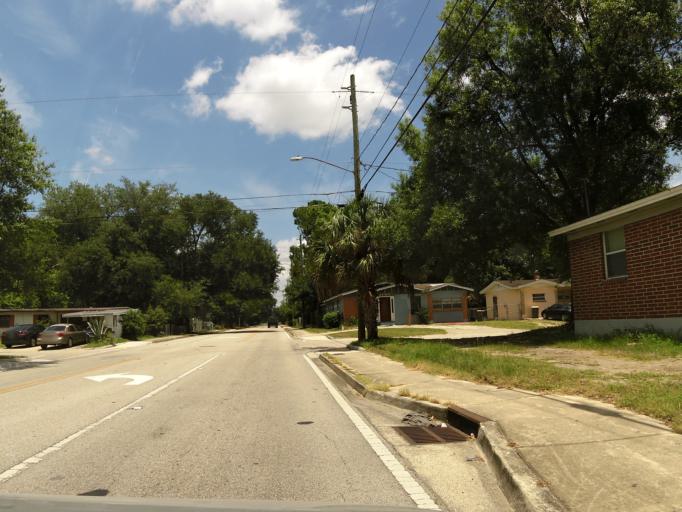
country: US
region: Florida
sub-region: Duval County
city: Jacksonville
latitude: 30.3523
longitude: -81.6970
